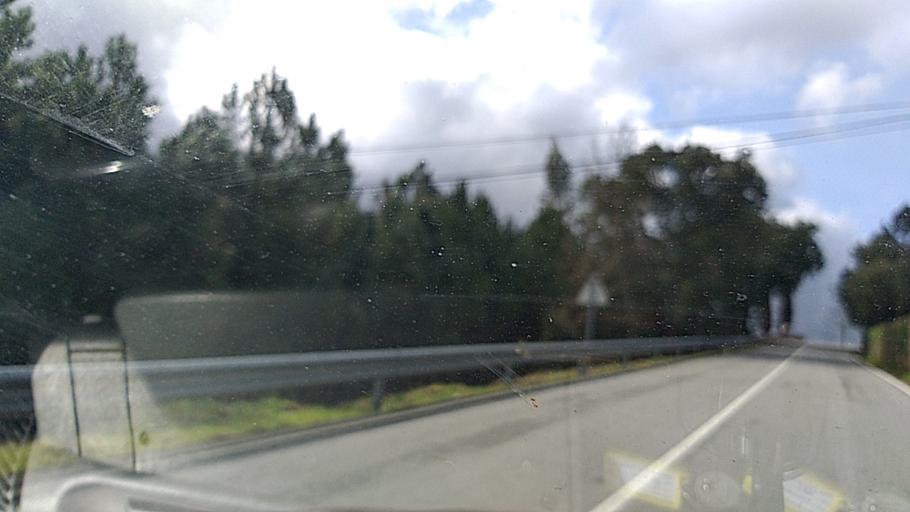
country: PT
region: Viseu
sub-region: Satao
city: Satao
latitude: 40.6683
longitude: -7.6895
